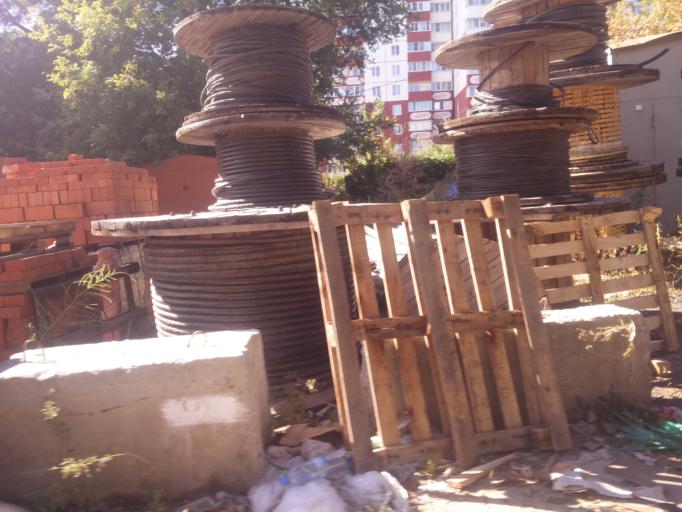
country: RU
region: Voronezj
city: Voronezh
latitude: 51.6476
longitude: 39.1604
